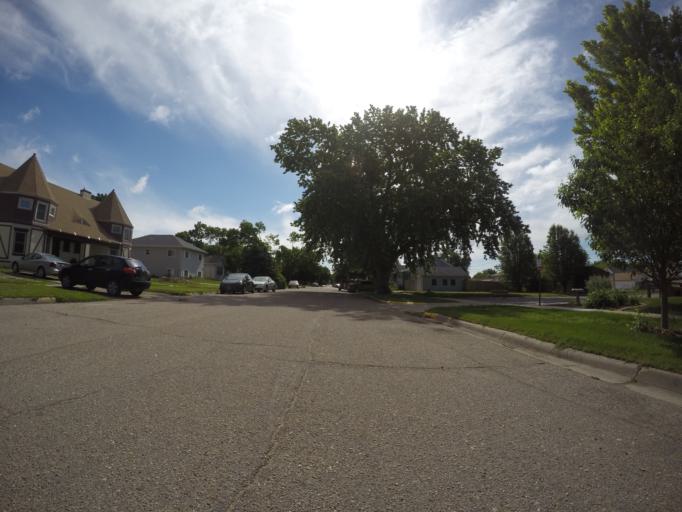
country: US
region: Nebraska
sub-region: Buffalo County
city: Kearney
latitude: 40.7037
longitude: -99.0935
